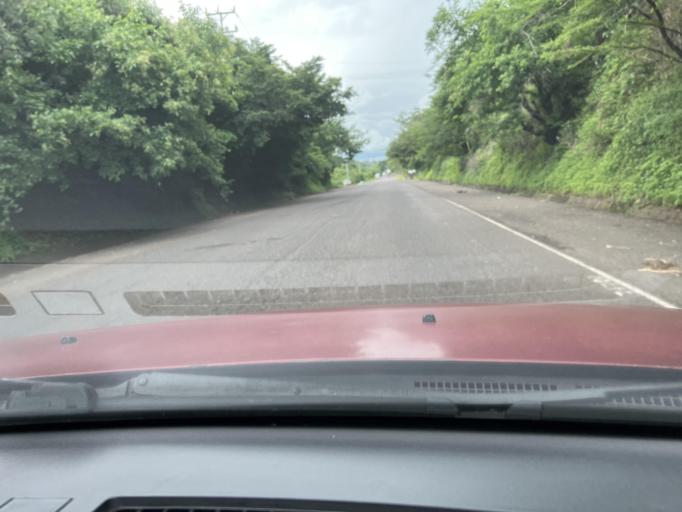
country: SV
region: La Union
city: San Alejo
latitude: 13.4213
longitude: -87.8861
